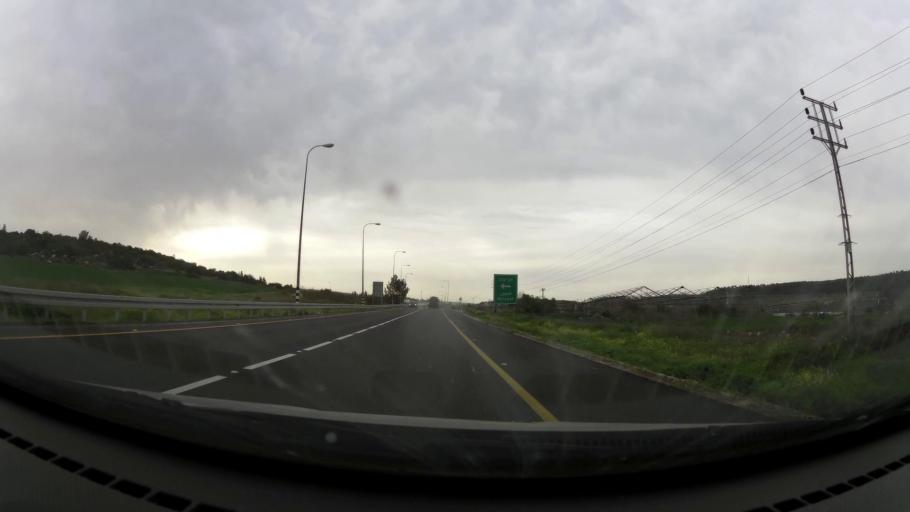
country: IL
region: Jerusalem
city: Bet Shemesh
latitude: 31.6772
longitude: 35.0051
